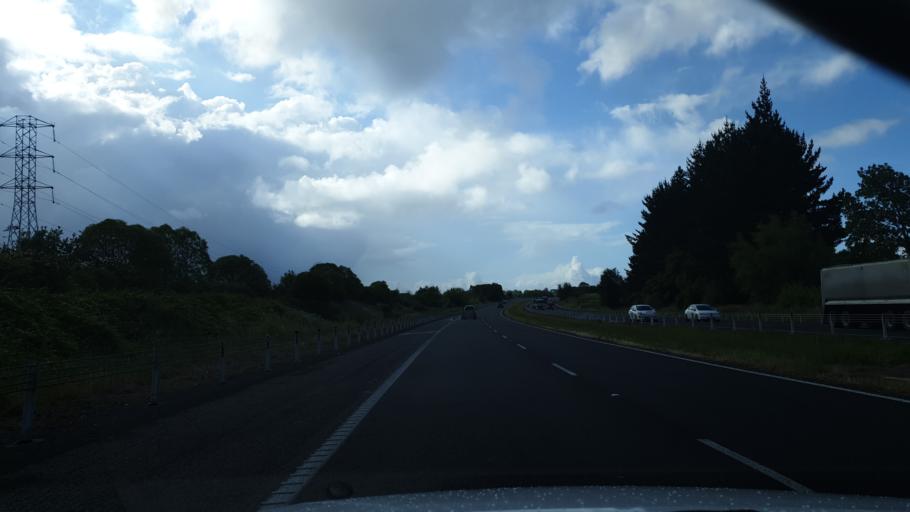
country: NZ
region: Auckland
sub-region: Auckland
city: Pukekohe East
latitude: -37.2429
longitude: 175.0246
